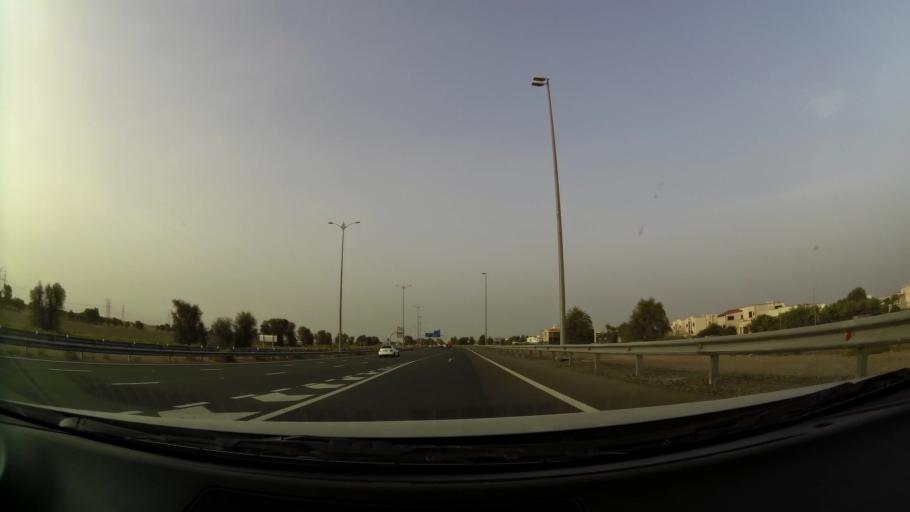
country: OM
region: Al Buraimi
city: Al Buraymi
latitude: 24.2792
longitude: 55.7290
